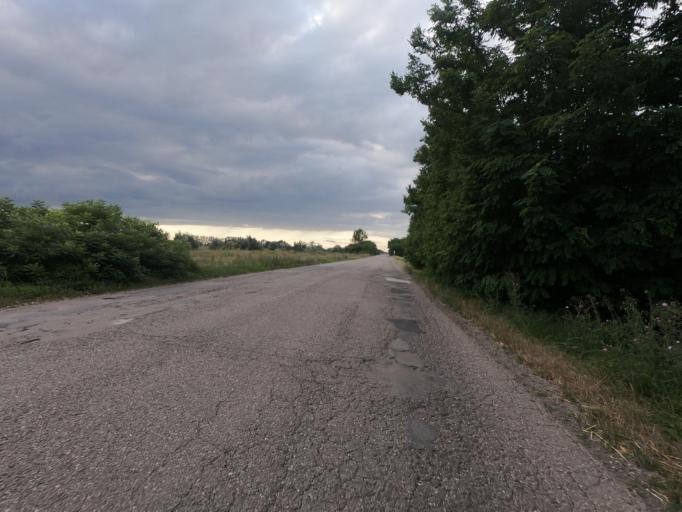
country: HU
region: Heves
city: Poroszlo
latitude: 47.6753
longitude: 20.6573
